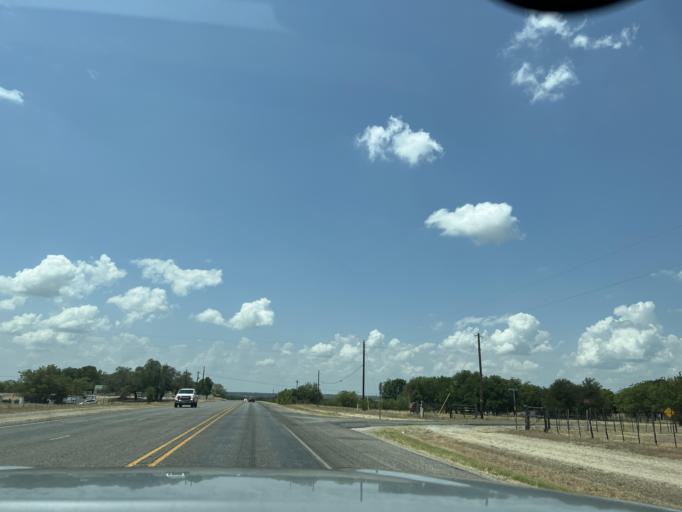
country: US
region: Texas
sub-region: Parker County
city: Springtown
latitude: 32.8948
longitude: -97.7309
